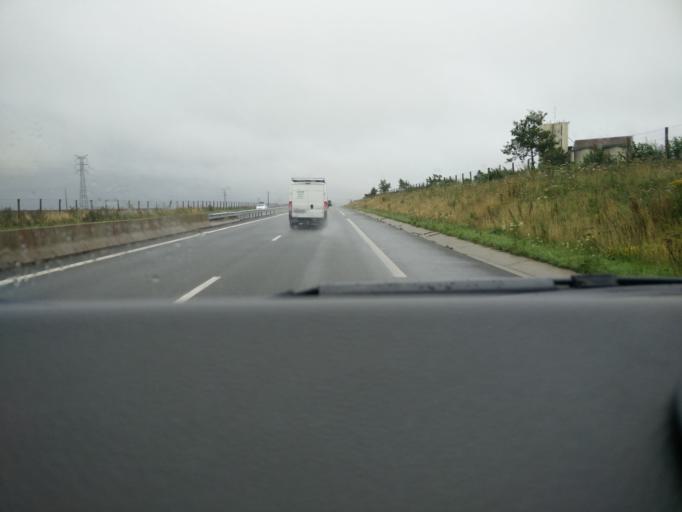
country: FR
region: Nord-Pas-de-Calais
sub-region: Departement du Pas-de-Calais
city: Marconnelle
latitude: 50.3673
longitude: 1.9582
